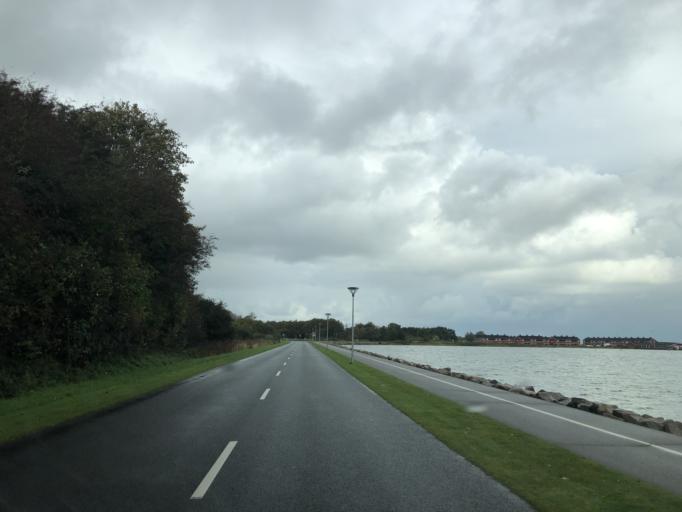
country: DK
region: Central Jutland
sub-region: Lemvig Kommune
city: Lemvig
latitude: 56.5597
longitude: 8.2950
